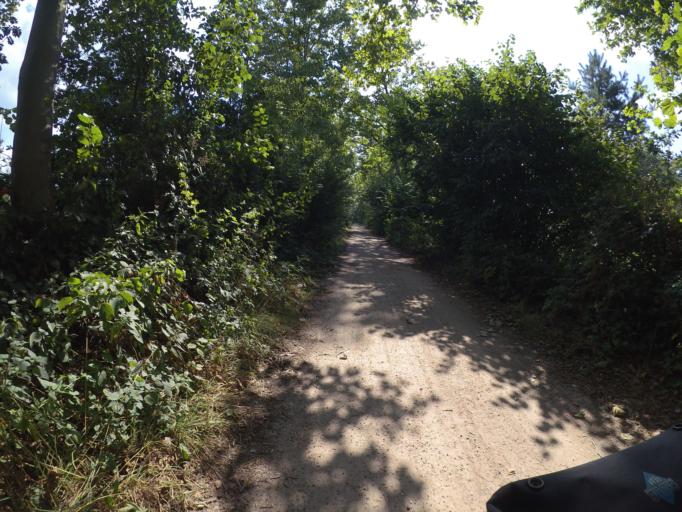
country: NL
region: North Brabant
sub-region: Gemeente Sint-Oedenrode
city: Sint-Oedenrode
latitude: 51.5870
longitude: 5.4427
